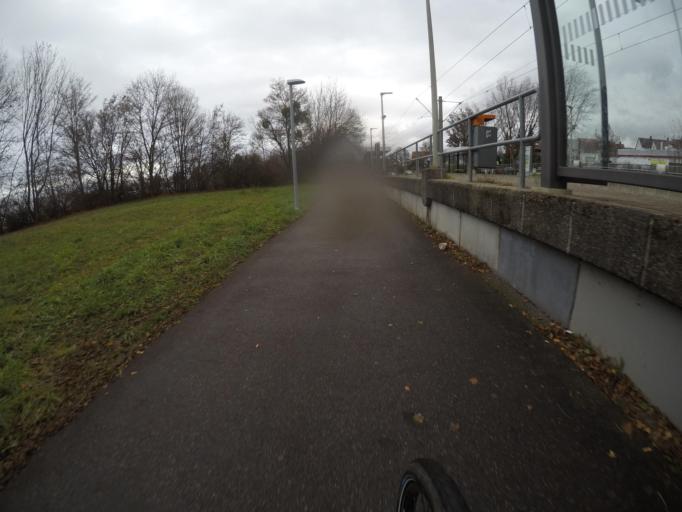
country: DE
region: Baden-Wuerttemberg
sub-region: Regierungsbezirk Stuttgart
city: Korntal
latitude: 48.8042
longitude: 9.1008
